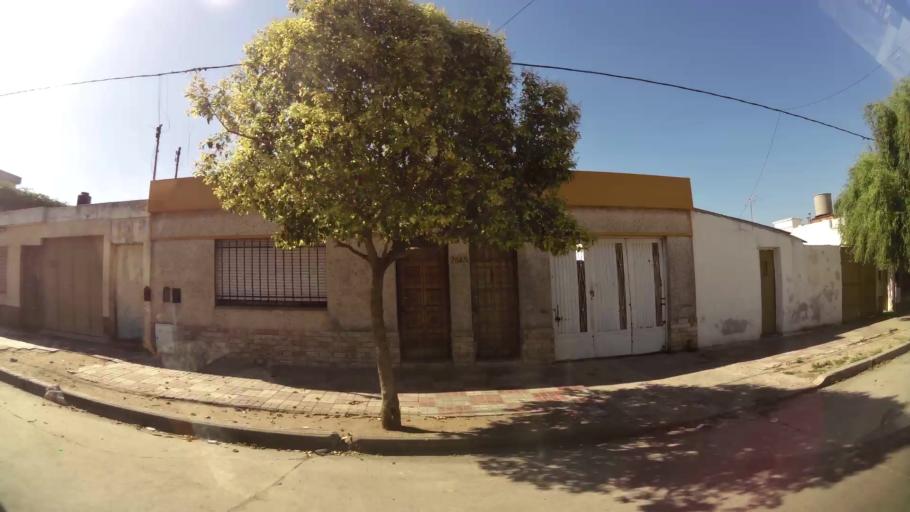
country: AR
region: Cordoba
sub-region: Departamento de Capital
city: Cordoba
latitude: -31.4146
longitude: -64.1484
